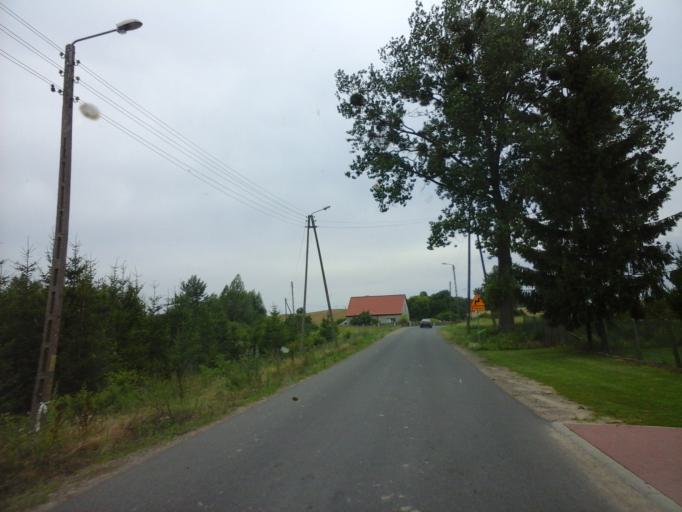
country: PL
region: West Pomeranian Voivodeship
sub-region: Powiat choszczenski
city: Krzecin
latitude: 53.0858
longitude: 15.5421
